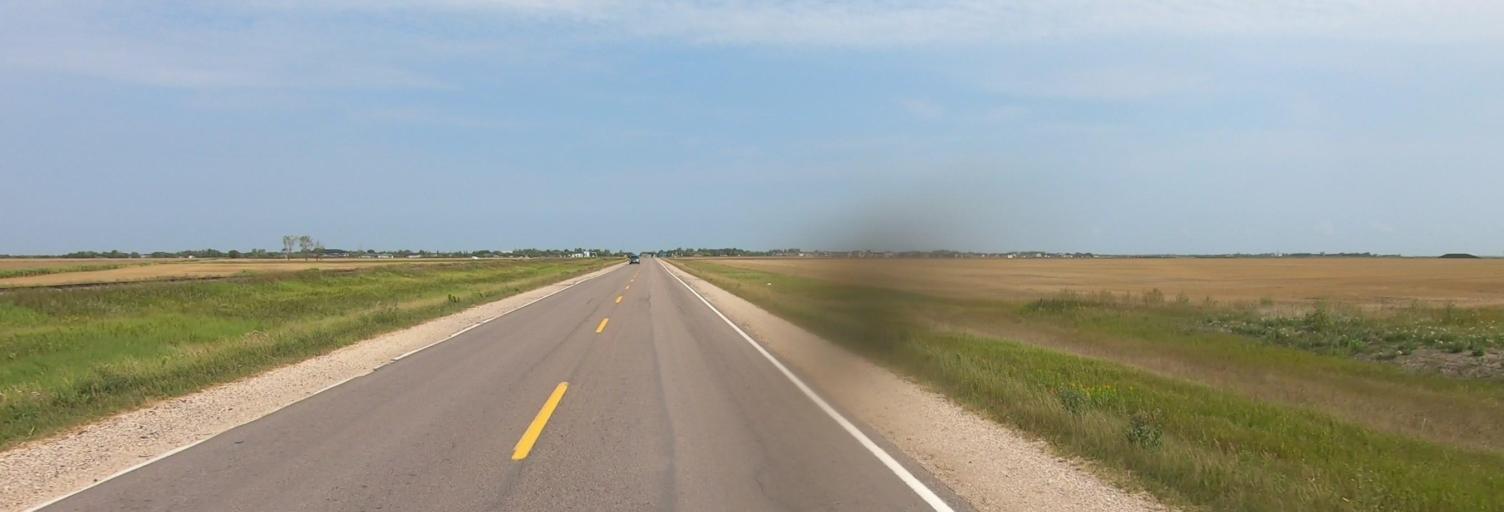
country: CA
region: Manitoba
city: Headingley
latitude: 49.6763
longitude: -97.2762
